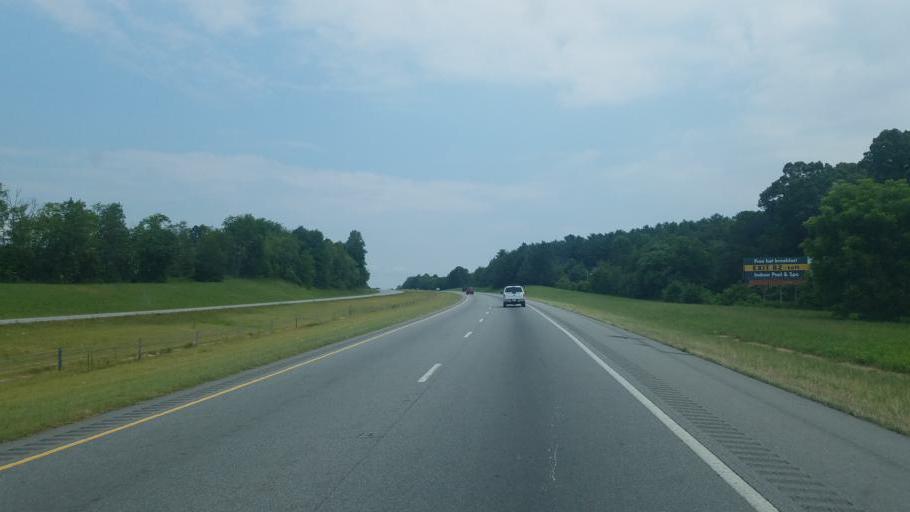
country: US
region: North Carolina
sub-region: Yadkin County
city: Yadkinville
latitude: 36.0335
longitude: -80.8186
